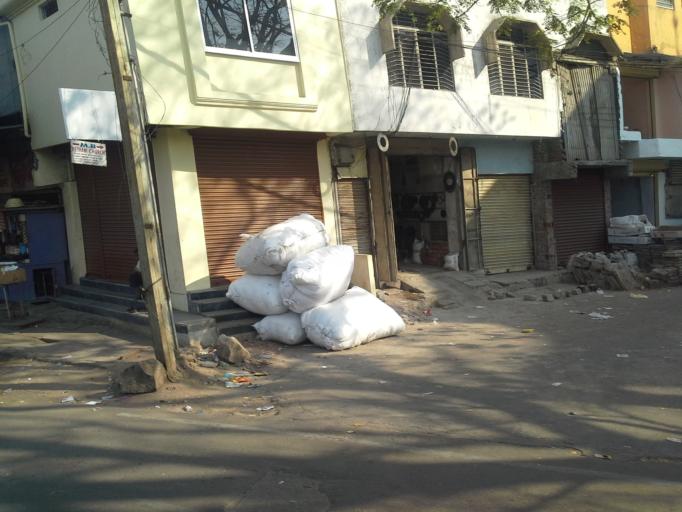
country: IN
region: Telangana
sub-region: Hyderabad
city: Hyderabad
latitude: 17.3712
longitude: 78.4780
